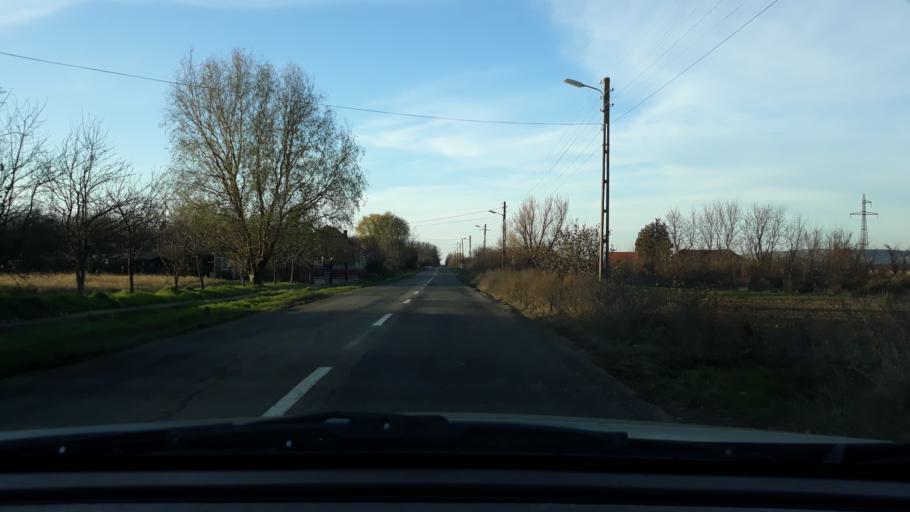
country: RO
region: Bihor
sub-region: Comuna Balc
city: Balc
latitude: 47.2775
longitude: 22.4805
